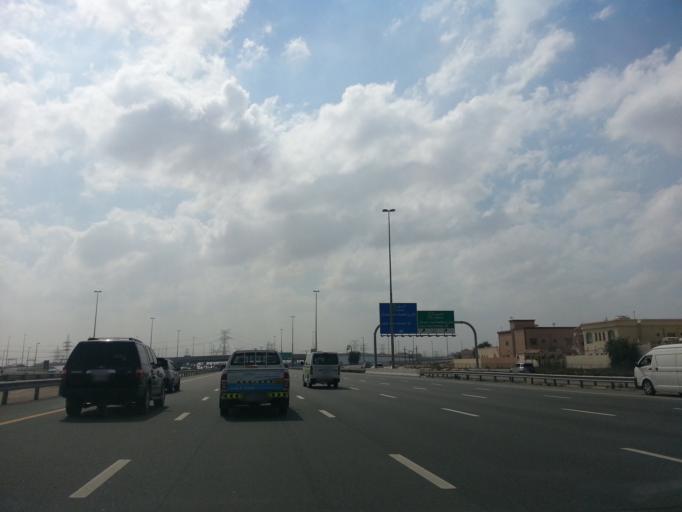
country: AE
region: Dubai
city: Dubai
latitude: 25.1496
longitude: 55.2612
